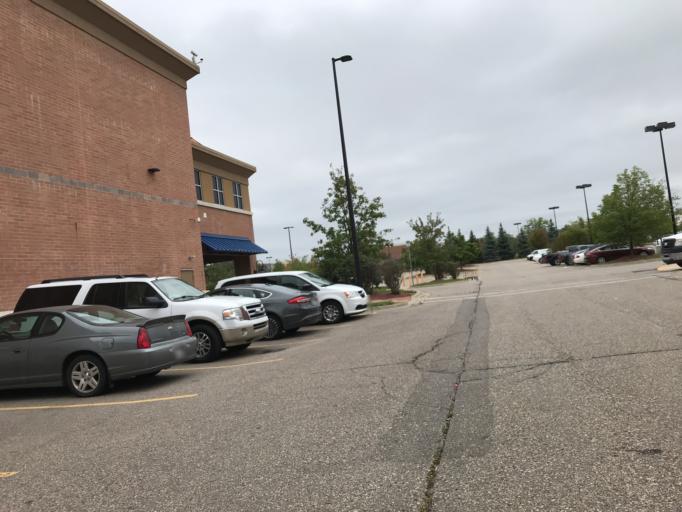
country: US
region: Michigan
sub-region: Oakland County
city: Farmington Hills
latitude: 42.5231
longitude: -83.3530
